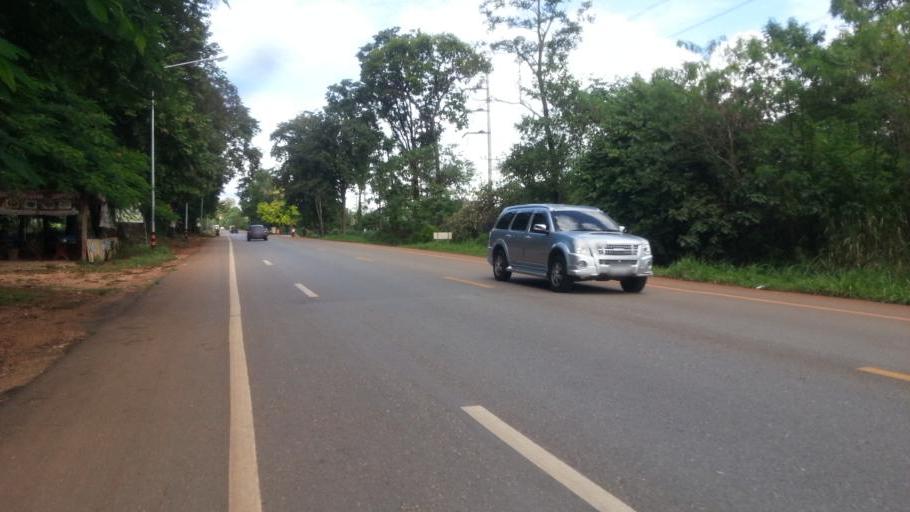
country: TH
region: Kanchanaburi
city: Sai Yok
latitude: 14.1166
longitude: 99.1875
